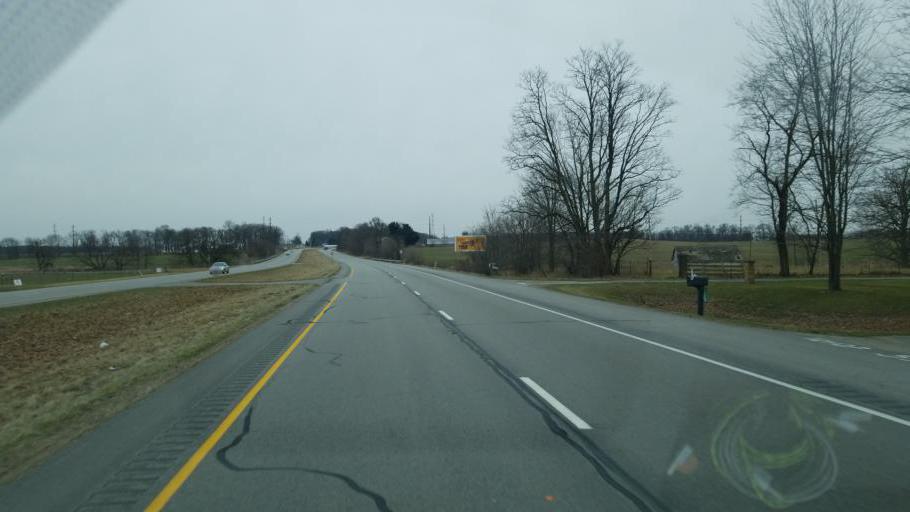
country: US
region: Indiana
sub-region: Marshall County
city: Plymouth
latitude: 41.2968
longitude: -86.2742
